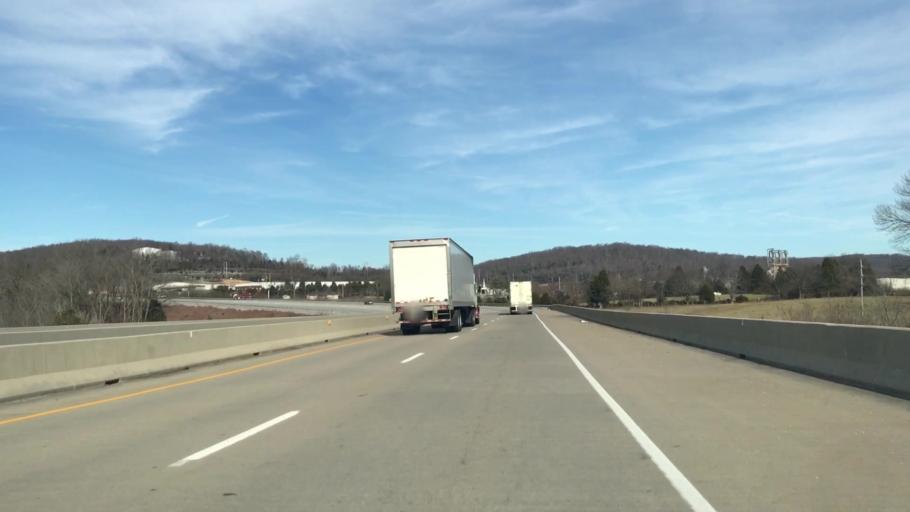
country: US
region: Kentucky
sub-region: Pulaski County
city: Somerset
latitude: 37.0432
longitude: -84.5851
